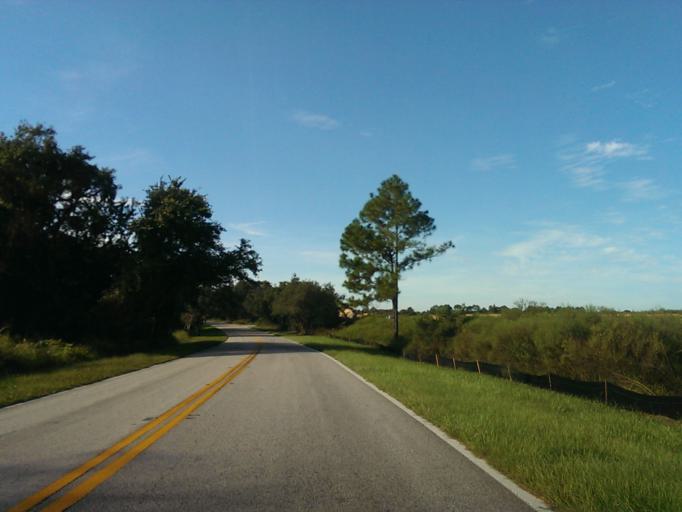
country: US
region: Florida
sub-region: Polk County
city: Citrus Ridge
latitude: 28.4029
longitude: -81.6376
